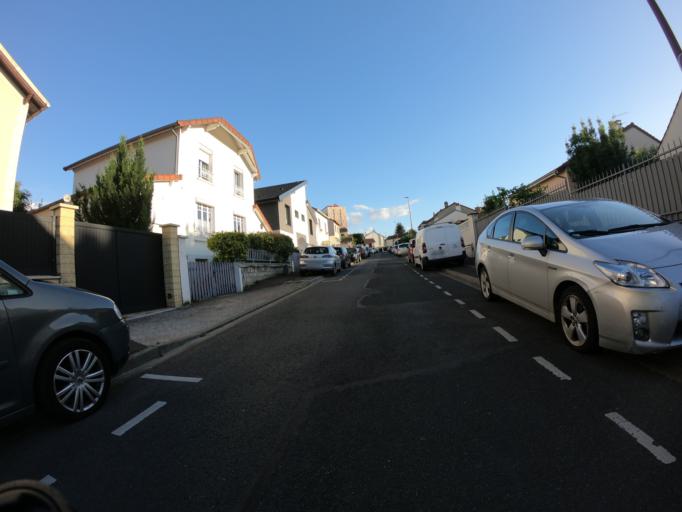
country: FR
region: Ile-de-France
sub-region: Departement du Val-de-Marne
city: Fresnes
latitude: 48.7559
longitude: 2.3195
